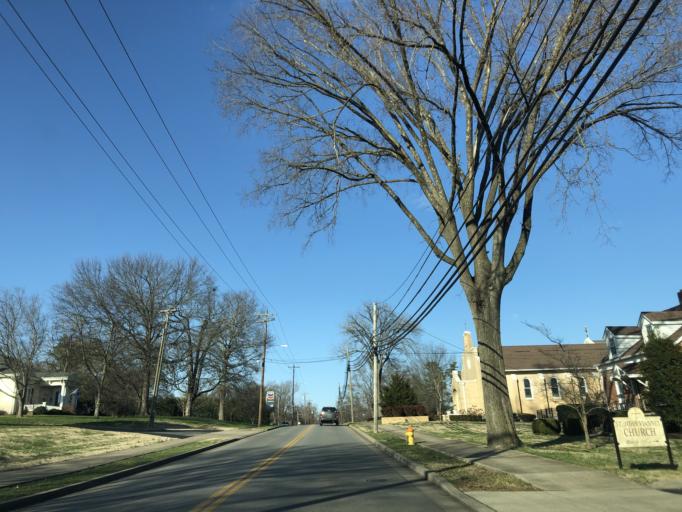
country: US
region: Tennessee
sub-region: Sumner County
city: Gallatin
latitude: 36.3947
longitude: -86.4467
